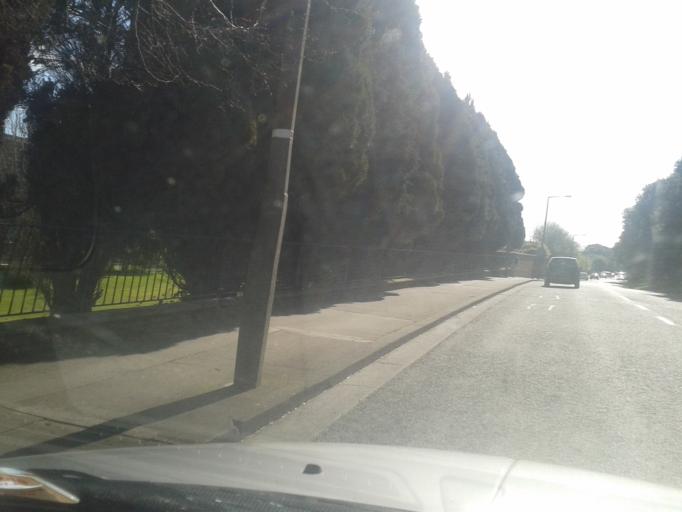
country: IE
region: Leinster
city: Raheny
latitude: 53.3783
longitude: -6.1737
